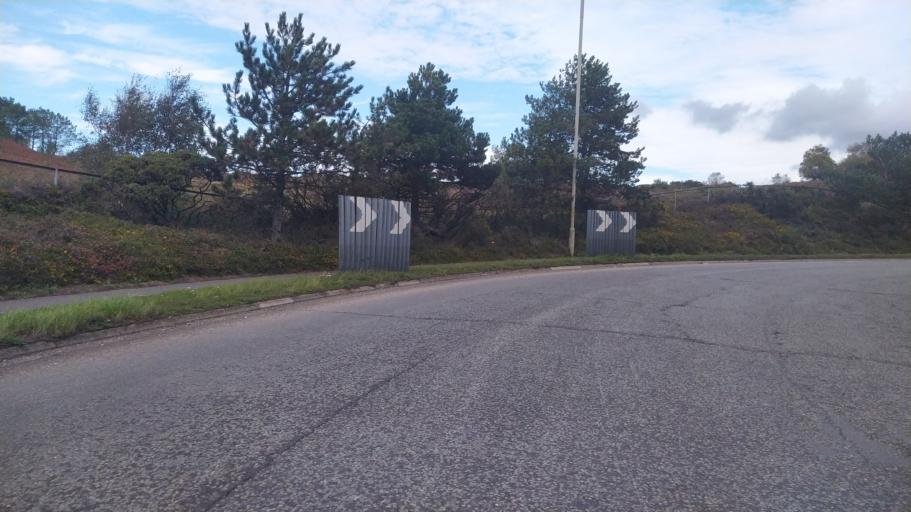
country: GB
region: England
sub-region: Poole
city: Canford Heath
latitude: 50.7541
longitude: -1.9493
